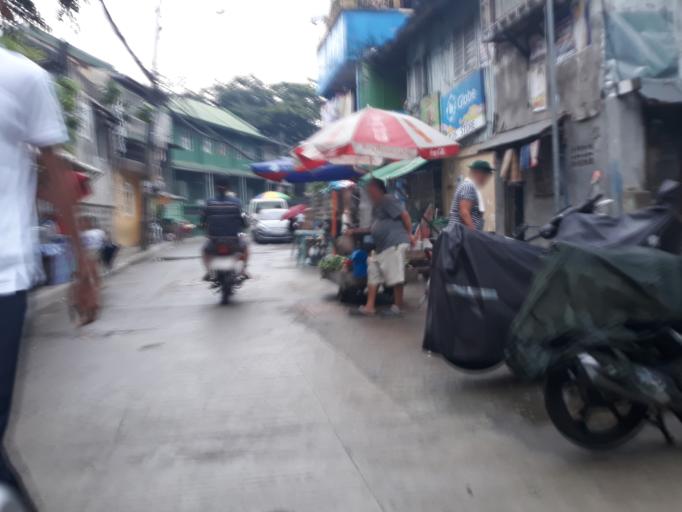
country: PH
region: Metro Manila
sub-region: San Juan
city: San Juan
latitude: 14.6104
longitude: 121.0224
